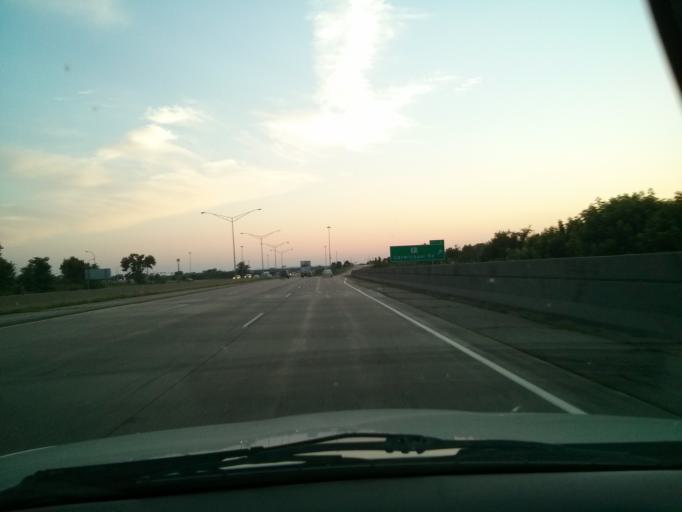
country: US
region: Wisconsin
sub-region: Saint Croix County
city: Hudson
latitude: 44.9640
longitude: -92.7134
